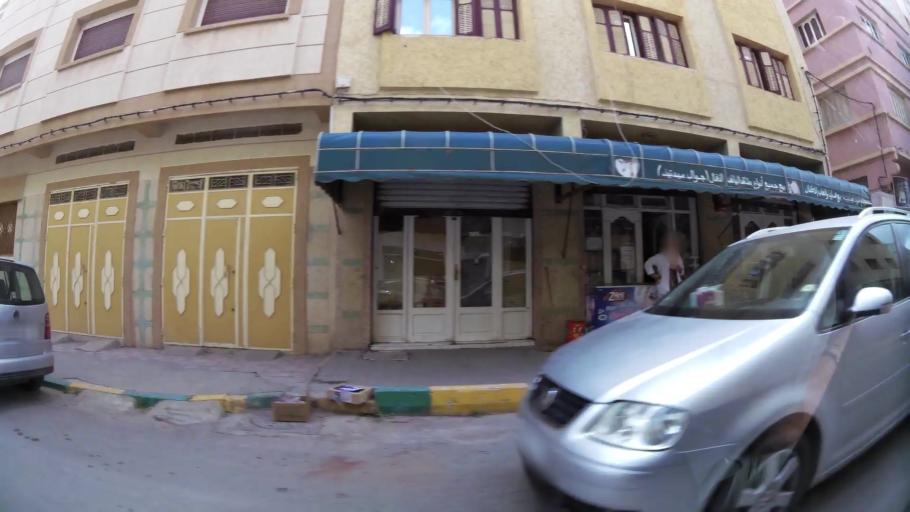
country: MA
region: Oriental
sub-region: Nador
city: Nador
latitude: 35.1704
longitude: -2.9220
